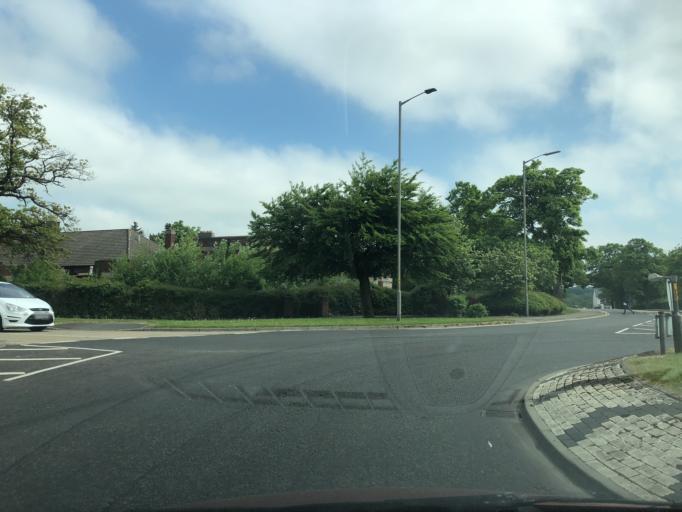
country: GB
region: England
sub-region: North Yorkshire
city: Catterick Garrison
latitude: 54.3799
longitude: -1.7246
